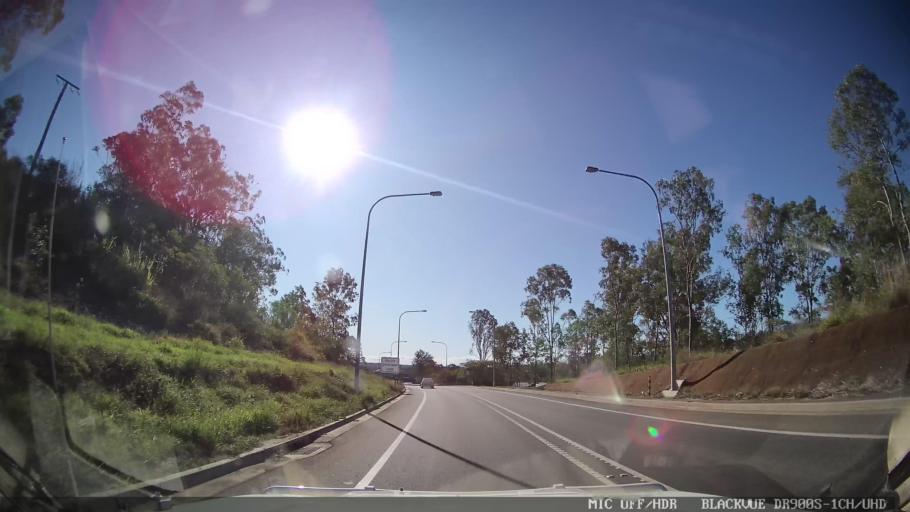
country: AU
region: Queensland
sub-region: Bundaberg
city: Sharon
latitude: -24.9959
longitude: 151.9604
